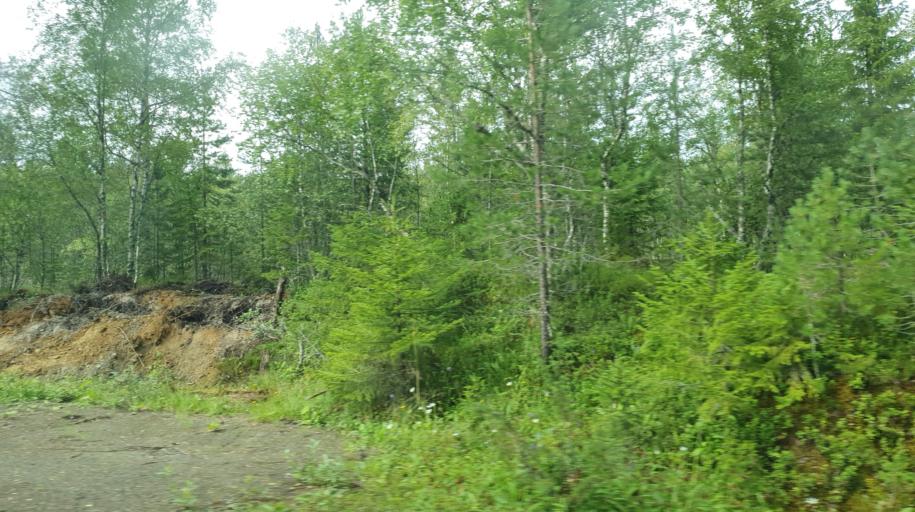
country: NO
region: Nord-Trondelag
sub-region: Levanger
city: Skogn
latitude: 63.5587
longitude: 11.1696
